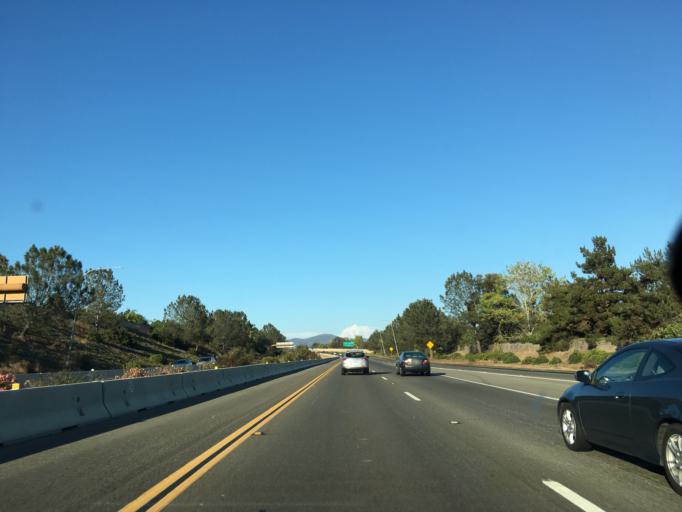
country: US
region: California
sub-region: San Diego County
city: Fairbanks Ranch
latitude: 32.9453
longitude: -117.2111
